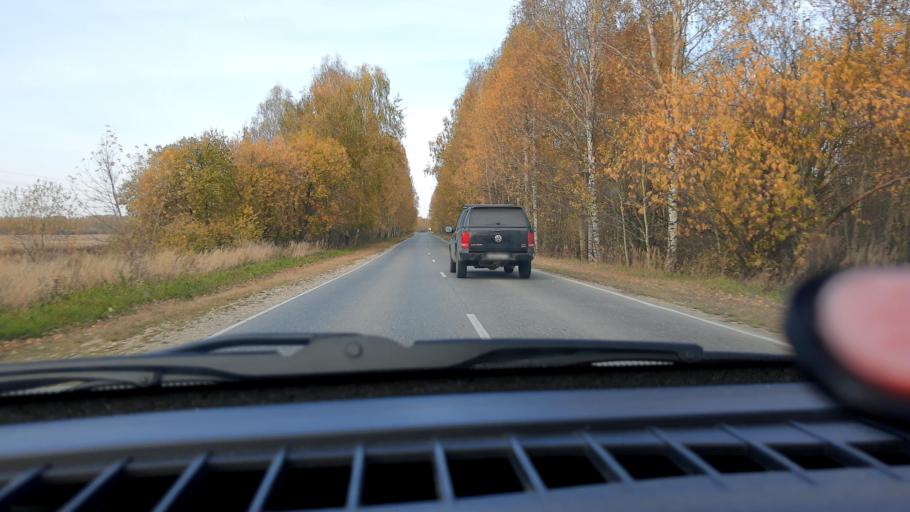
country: RU
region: Nizjnij Novgorod
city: Neklyudovo
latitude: 56.5216
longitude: 43.8357
